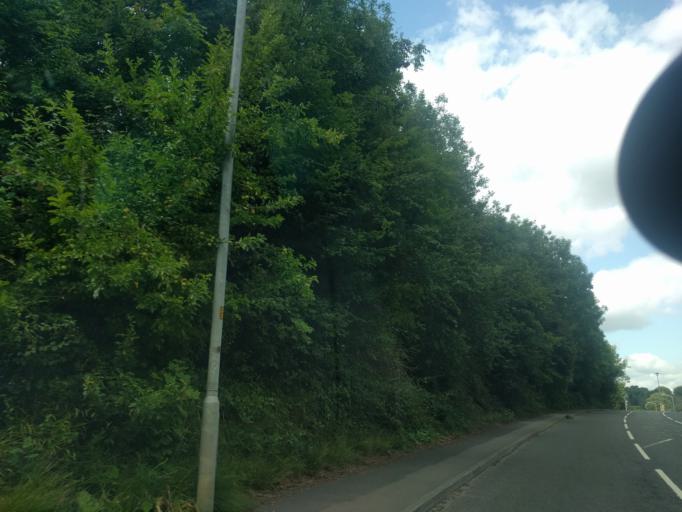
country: GB
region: England
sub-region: Wiltshire
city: Corsham
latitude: 51.4264
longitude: -2.1941
